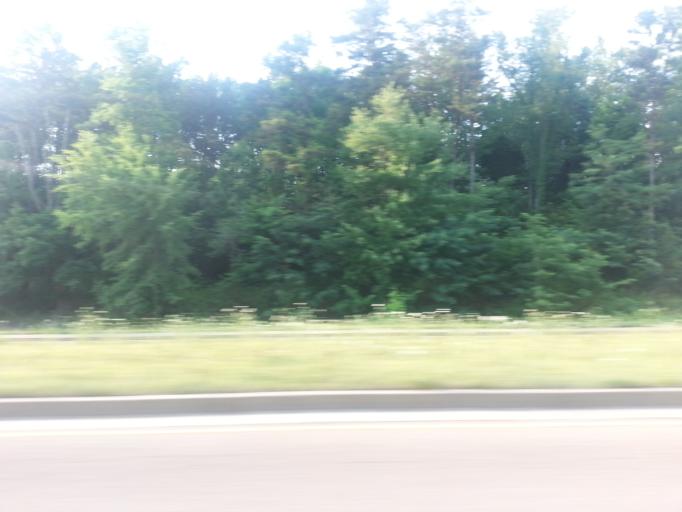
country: US
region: Tennessee
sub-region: Knox County
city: Farragut
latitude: 35.9452
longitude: -84.1089
